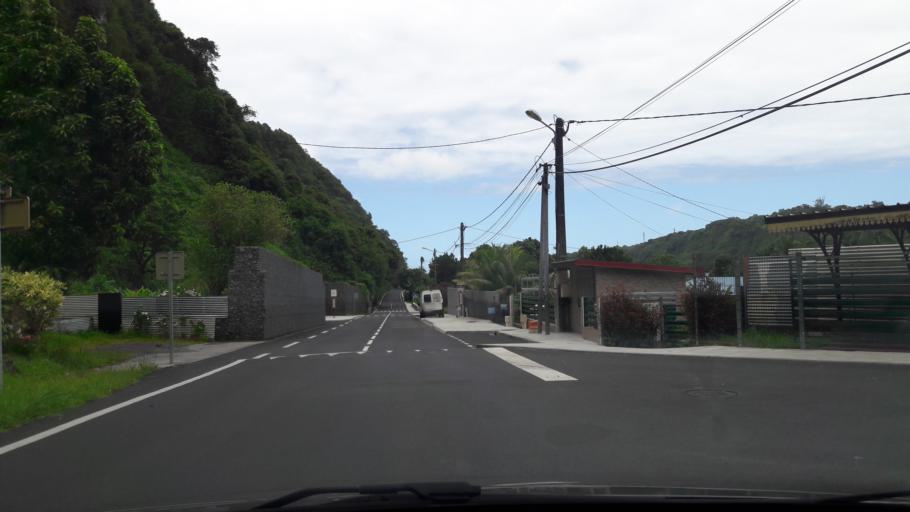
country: RE
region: Reunion
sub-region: Reunion
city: Saint-Andre
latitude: -20.9889
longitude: 55.6161
